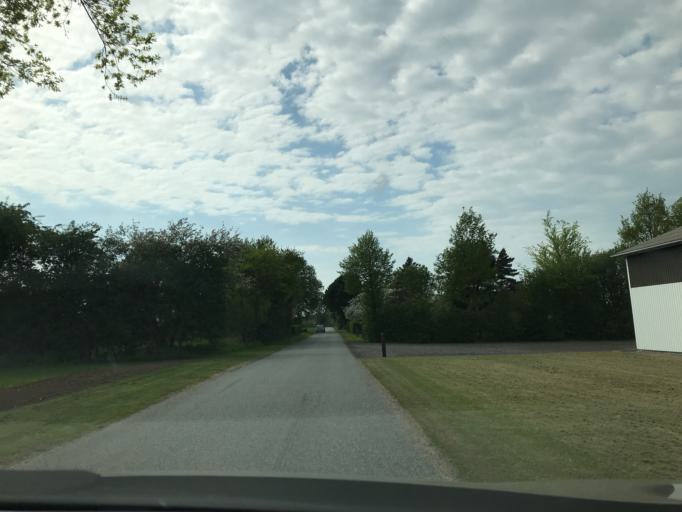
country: DK
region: South Denmark
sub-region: Middelfart Kommune
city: Norre Aby
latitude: 55.3629
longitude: 9.8487
